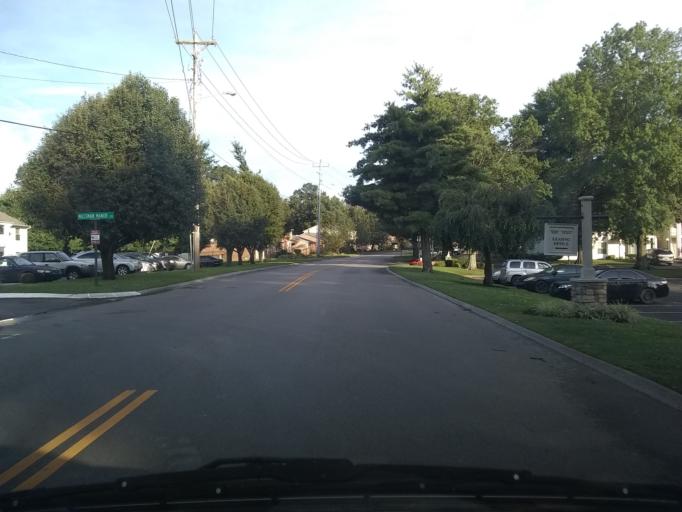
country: US
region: Tennessee
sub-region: Davidson County
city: Nashville
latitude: 36.1323
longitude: -86.7010
